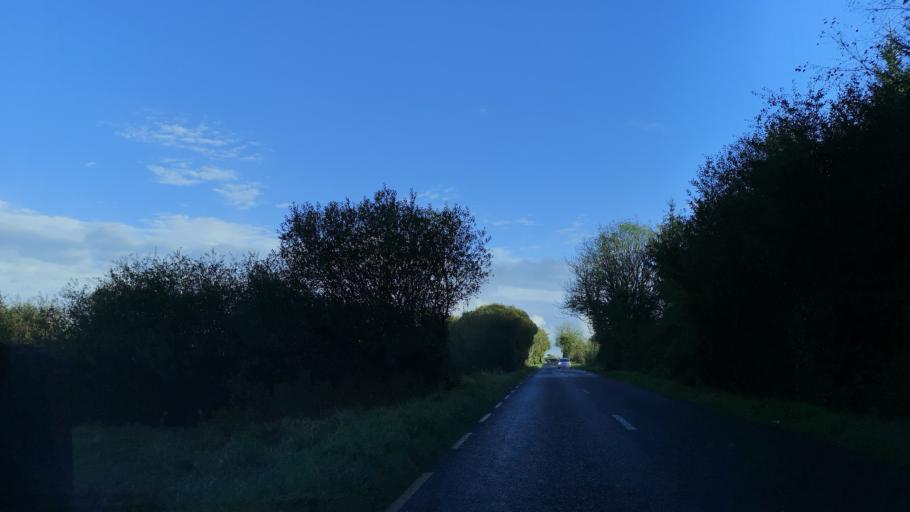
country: IE
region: Connaught
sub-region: Roscommon
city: Castlerea
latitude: 53.8124
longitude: -8.5276
